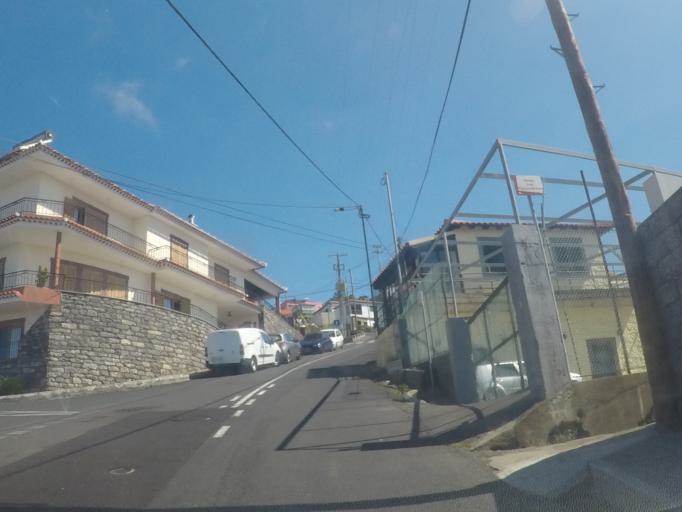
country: PT
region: Madeira
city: Camara de Lobos
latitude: 32.6732
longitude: -16.9646
